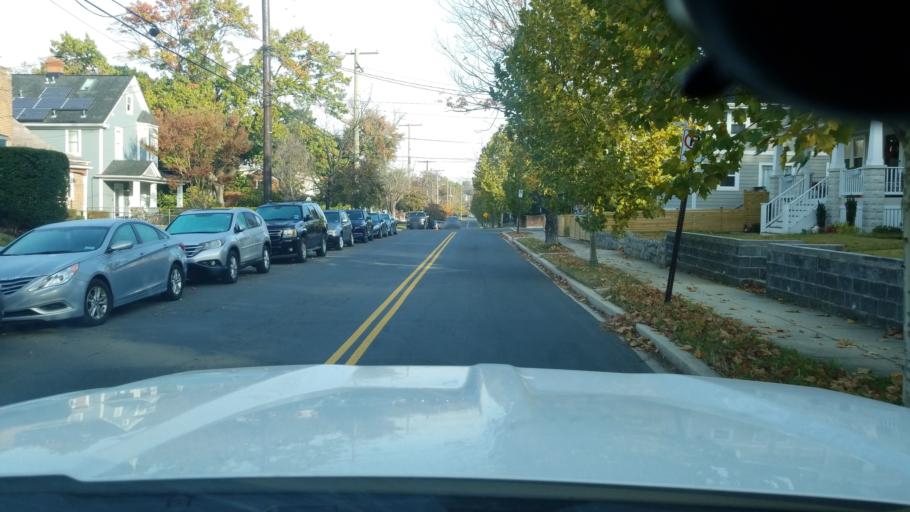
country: US
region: Maryland
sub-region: Prince George's County
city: Mount Rainier
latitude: 38.9402
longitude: -76.9742
